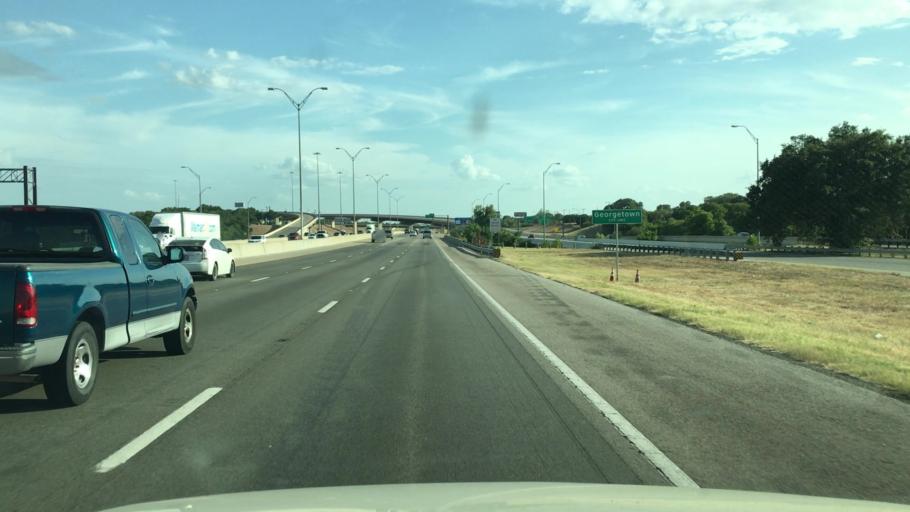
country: US
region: Texas
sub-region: Williamson County
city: Serenada
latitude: 30.6932
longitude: -97.6553
